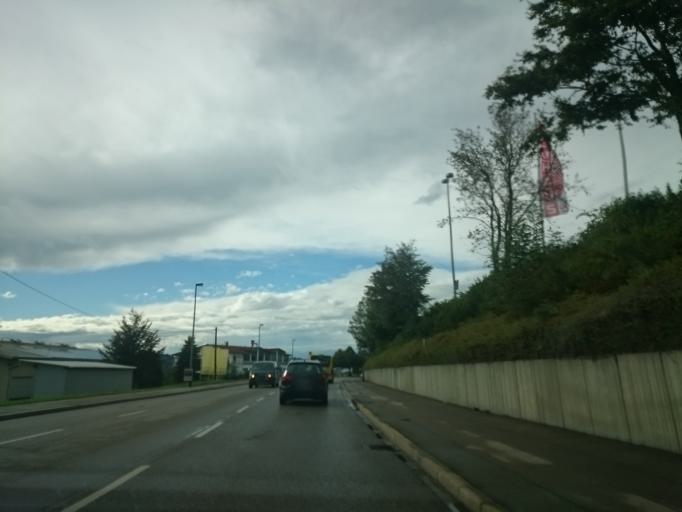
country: DE
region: Bavaria
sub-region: Swabia
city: Kempten (Allgaeu)
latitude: 47.7470
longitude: 10.3227
